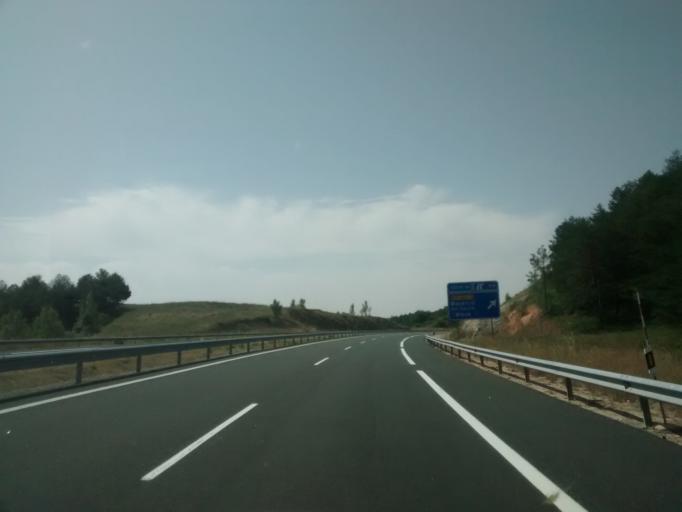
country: ES
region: Castille and Leon
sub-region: Provincia de Palencia
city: Aguilar de Campoo
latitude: 42.7311
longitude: -4.2880
